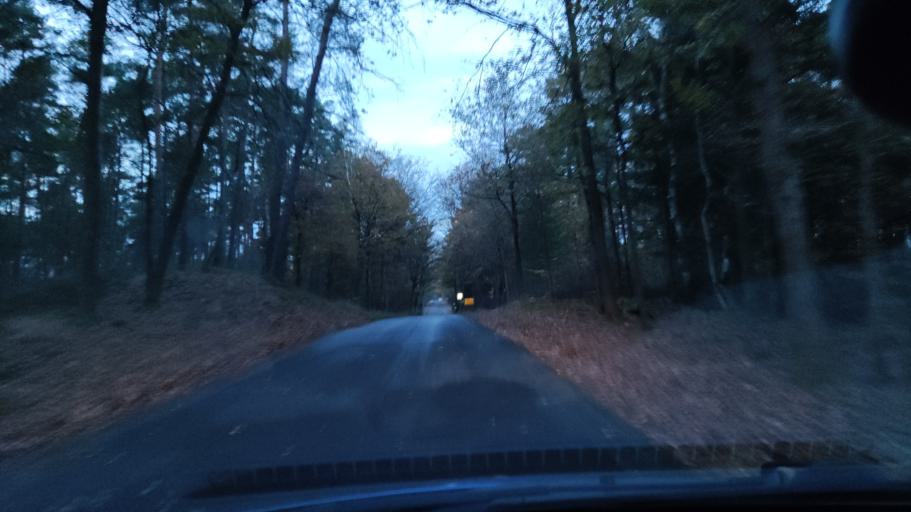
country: DE
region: Lower Saxony
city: Egestorf
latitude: 53.1589
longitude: 10.0349
